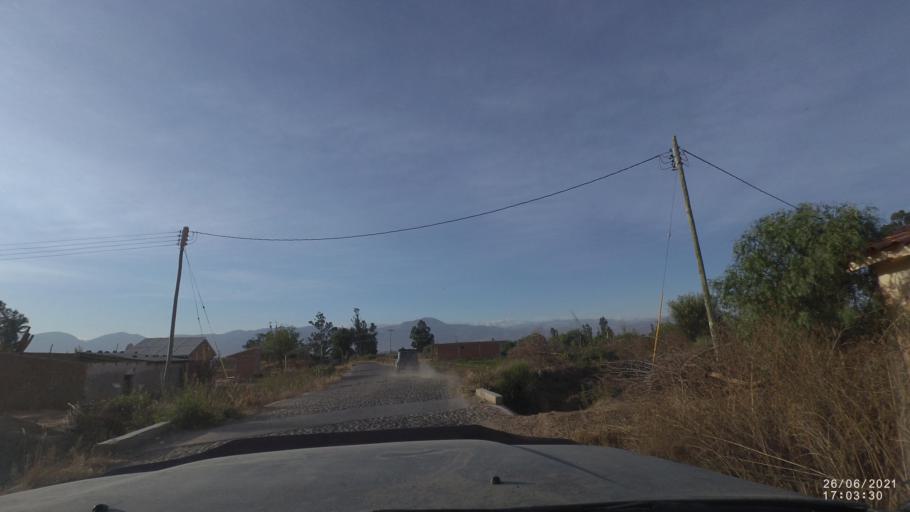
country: BO
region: Cochabamba
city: Cliza
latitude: -17.6418
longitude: -65.9117
